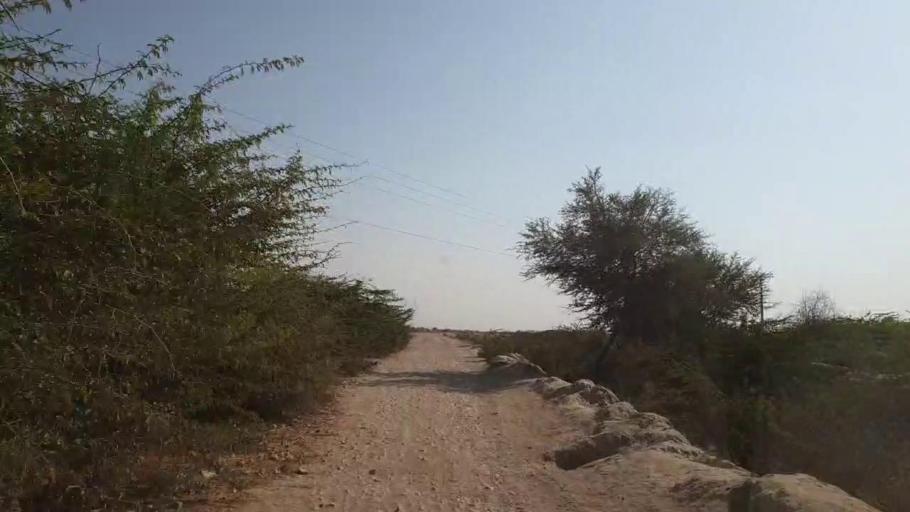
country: PK
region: Sindh
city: Nabisar
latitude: 25.0250
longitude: 69.4945
